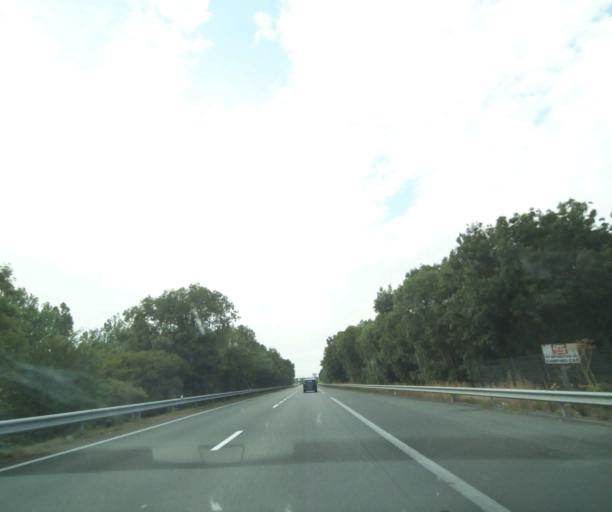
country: FR
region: Poitou-Charentes
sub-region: Departement de la Charente-Maritime
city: Chatelaillon-Plage
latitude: 46.0783
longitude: -1.0746
